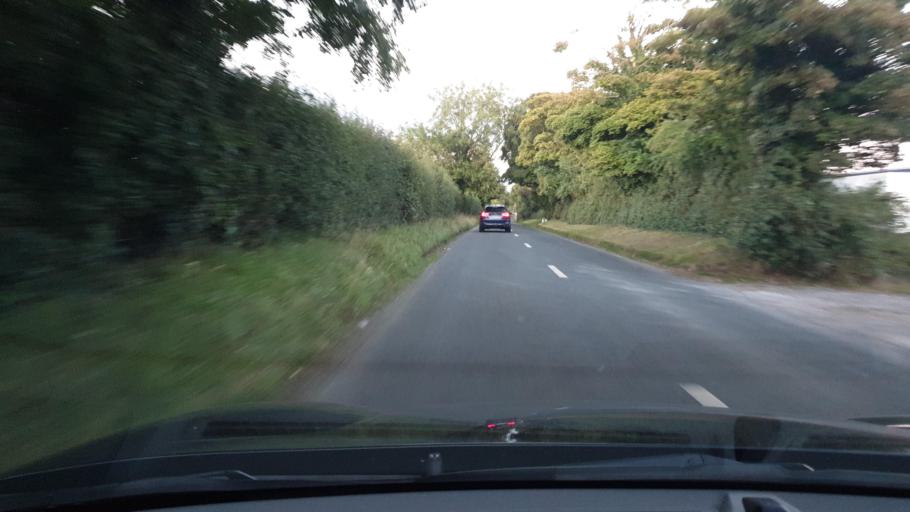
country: IE
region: Leinster
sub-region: Kildare
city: Clane
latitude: 53.3441
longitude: -6.7033
